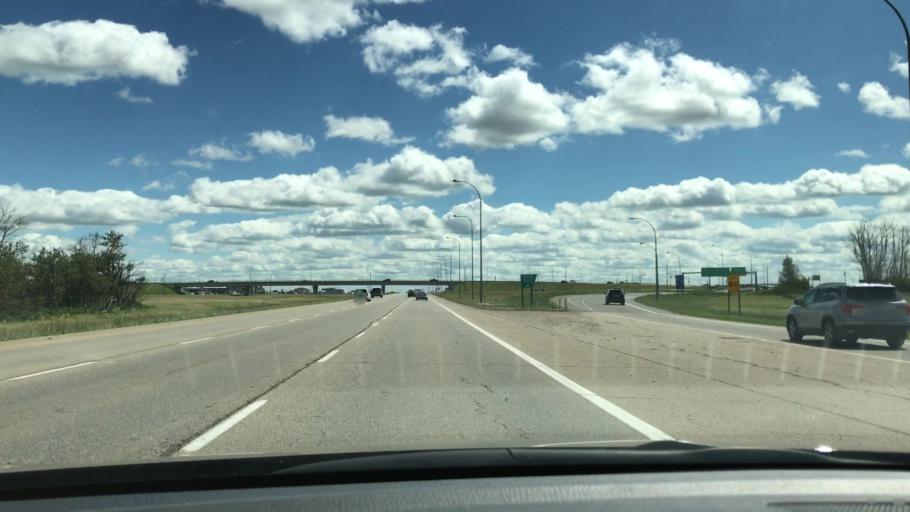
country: CA
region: Alberta
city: Leduc
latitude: 53.3140
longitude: -113.5503
